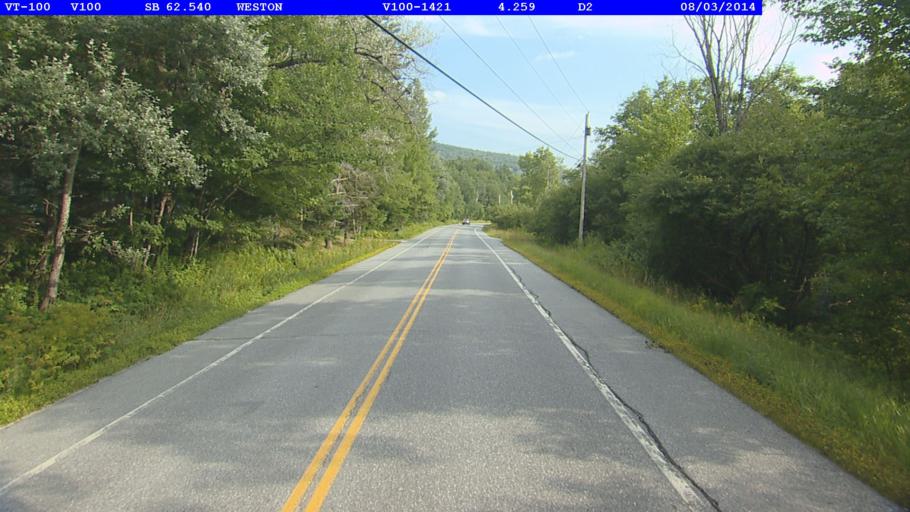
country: US
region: Vermont
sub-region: Windsor County
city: Chester
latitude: 43.3055
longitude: -72.7863
